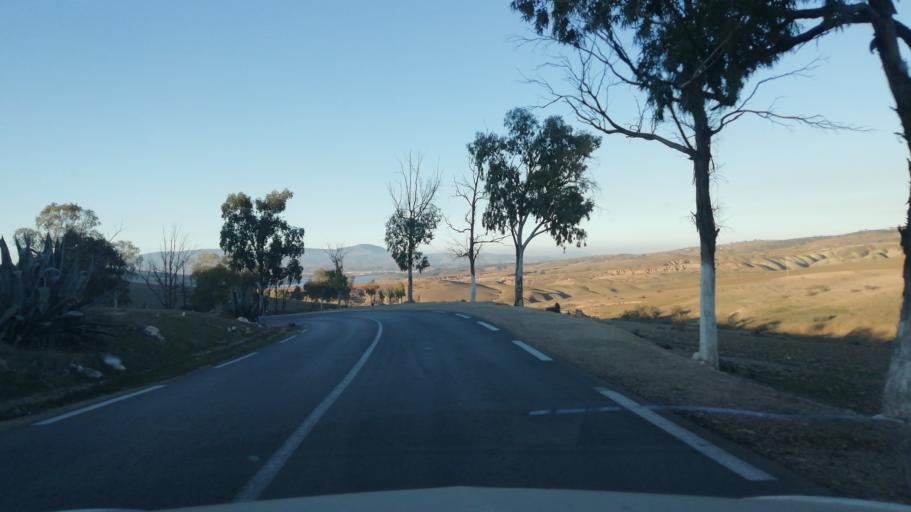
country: DZ
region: Tlemcen
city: Nedroma
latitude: 34.8250
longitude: -1.6386
